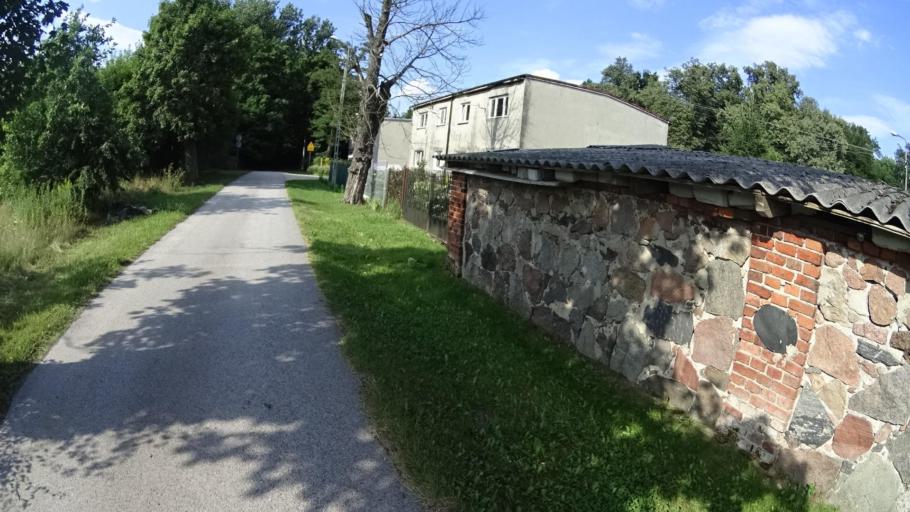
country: PL
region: Masovian Voivodeship
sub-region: Powiat piaseczynski
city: Lesznowola
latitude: 52.0230
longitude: 20.9043
